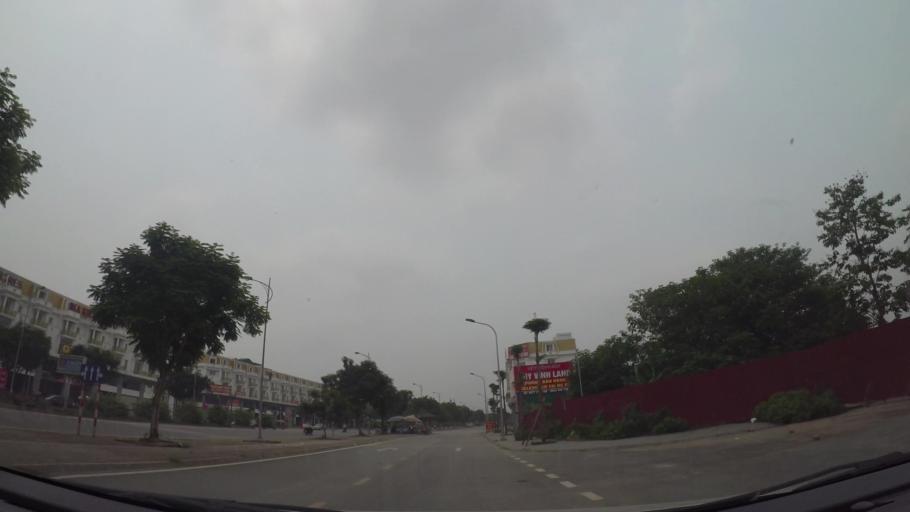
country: VN
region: Ha Noi
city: Ha Dong
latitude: 20.9834
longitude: 105.7413
